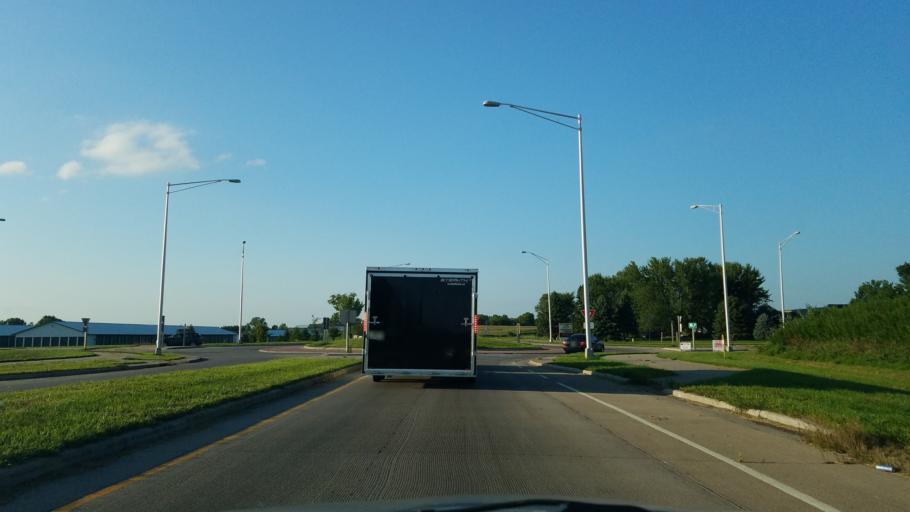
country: US
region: Wisconsin
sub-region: Saint Croix County
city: New Richmond
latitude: 45.0785
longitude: -92.5375
